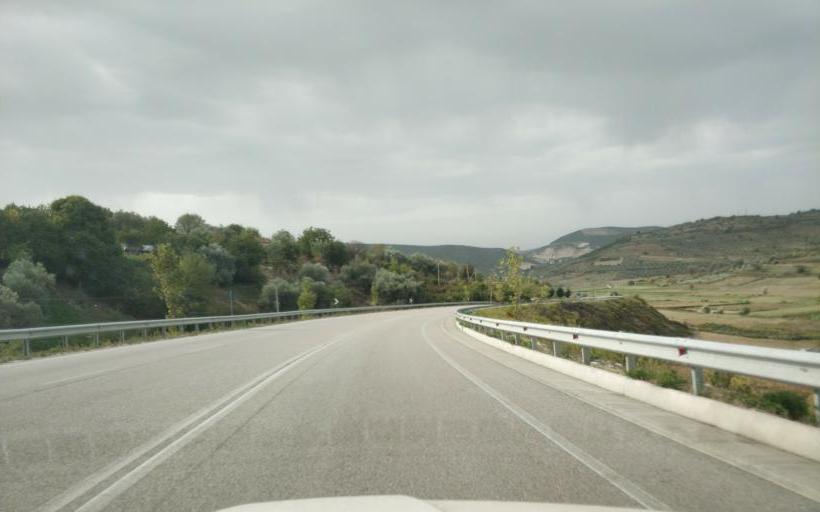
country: AL
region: Fier
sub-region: Rrethi i Mallakastres
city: Fratar
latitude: 40.4925
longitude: 19.8315
